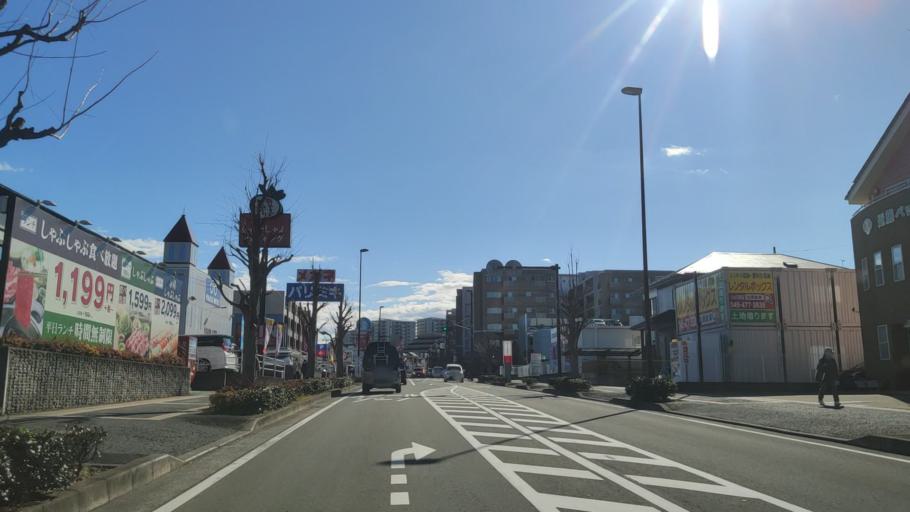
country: JP
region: Tokyo
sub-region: Machida-shi
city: Machida
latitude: 35.5252
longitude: 139.4983
